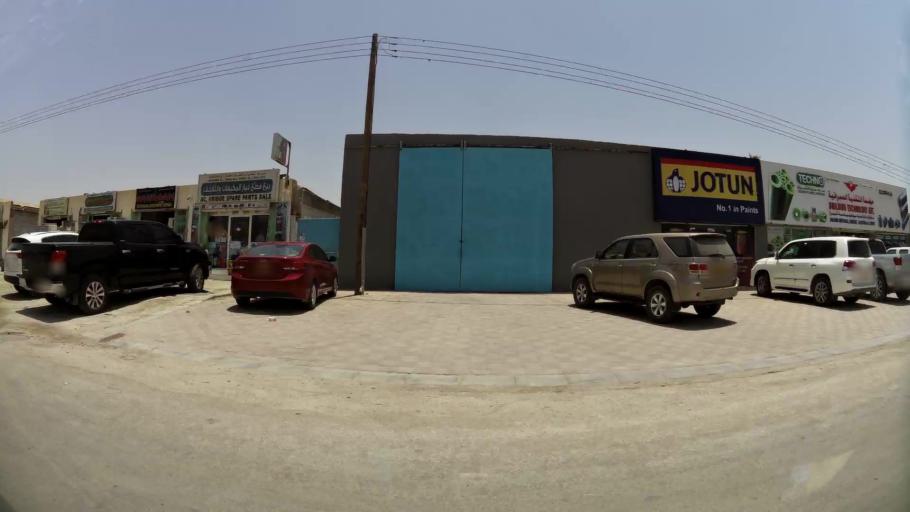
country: OM
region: Zufar
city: Salalah
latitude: 17.0218
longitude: 54.1150
